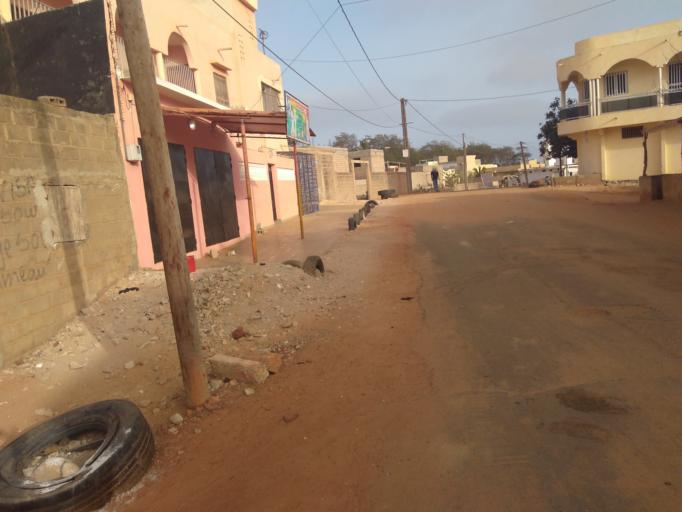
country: SN
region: Dakar
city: Pikine
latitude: 14.8025
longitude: -17.3413
